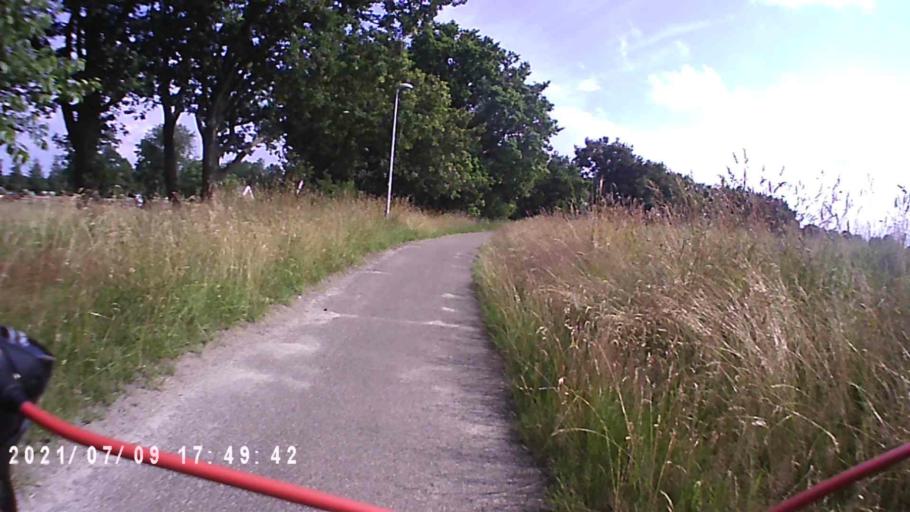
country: NL
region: Groningen
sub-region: Gemeente Vlagtwedde
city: Vlagtwedde
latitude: 53.0738
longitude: 7.0771
